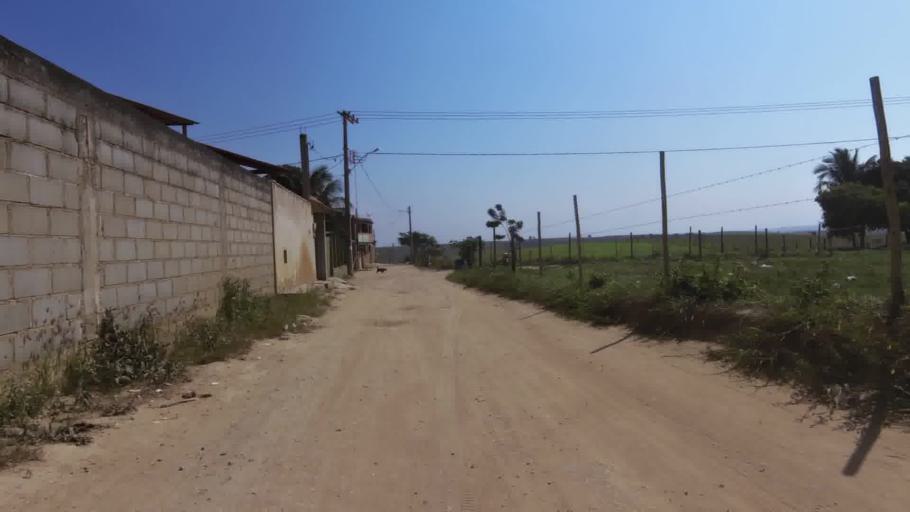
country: BR
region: Espirito Santo
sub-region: Marataizes
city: Marataizes
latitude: -21.0284
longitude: -40.8208
